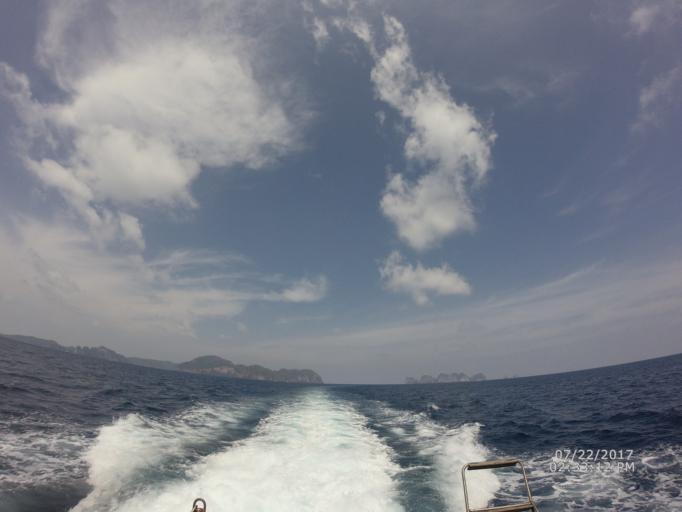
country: TH
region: Phangnga
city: Ban Phru Nai
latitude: 7.7414
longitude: 98.7102
